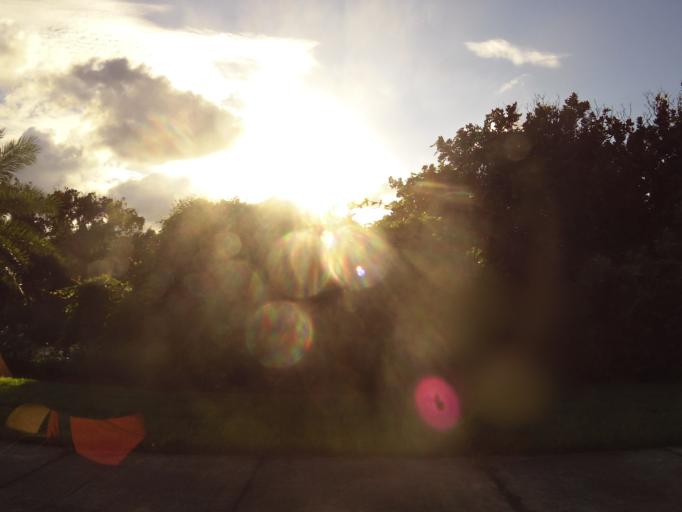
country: US
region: Florida
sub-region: Saint Johns County
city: Sawgrass
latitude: 30.1742
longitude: -81.3604
